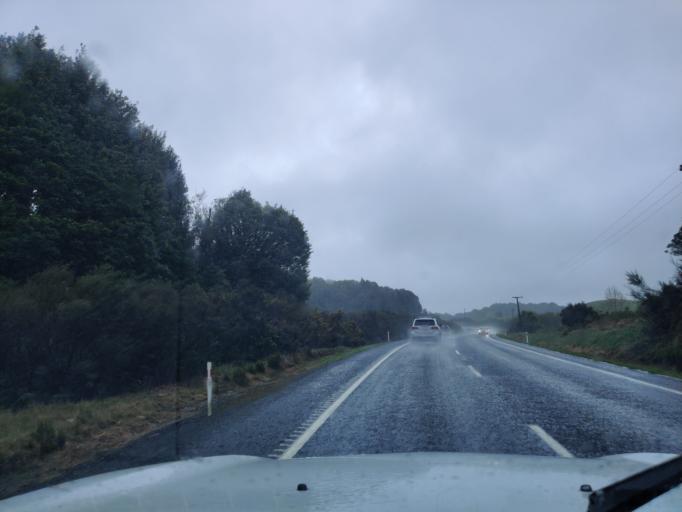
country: NZ
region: Bay of Plenty
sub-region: Rotorua District
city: Rotorua
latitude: -38.0354
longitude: 176.0280
